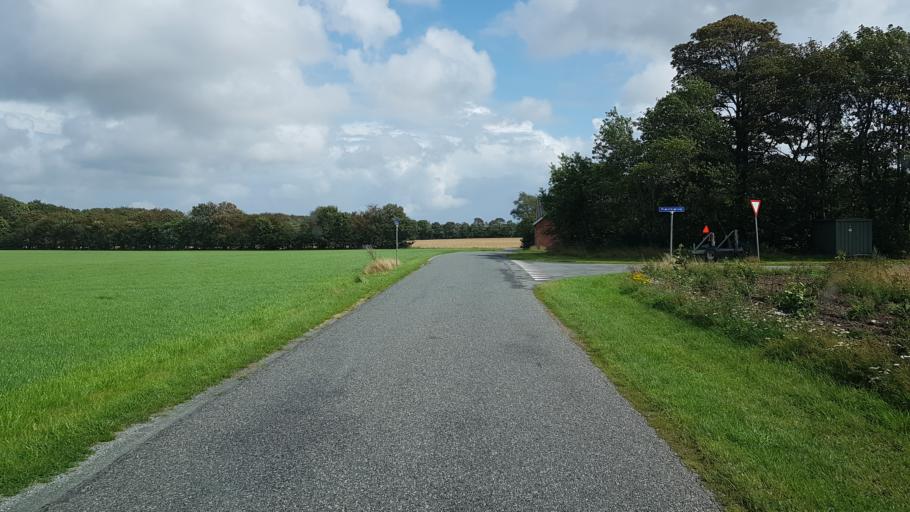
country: DK
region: South Denmark
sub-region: Vejen Kommune
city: Holsted
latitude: 55.4948
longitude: 8.9496
